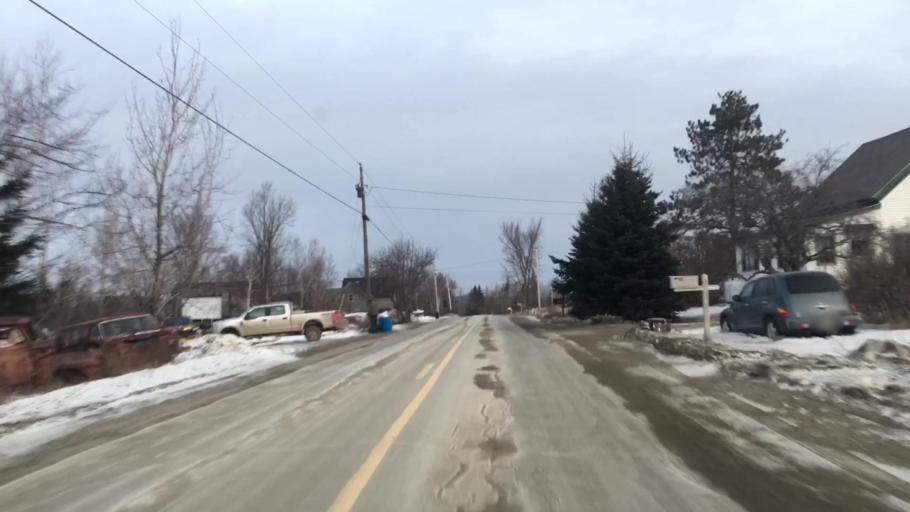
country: US
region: Maine
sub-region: Hancock County
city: Franklin
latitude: 44.7321
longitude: -68.3358
